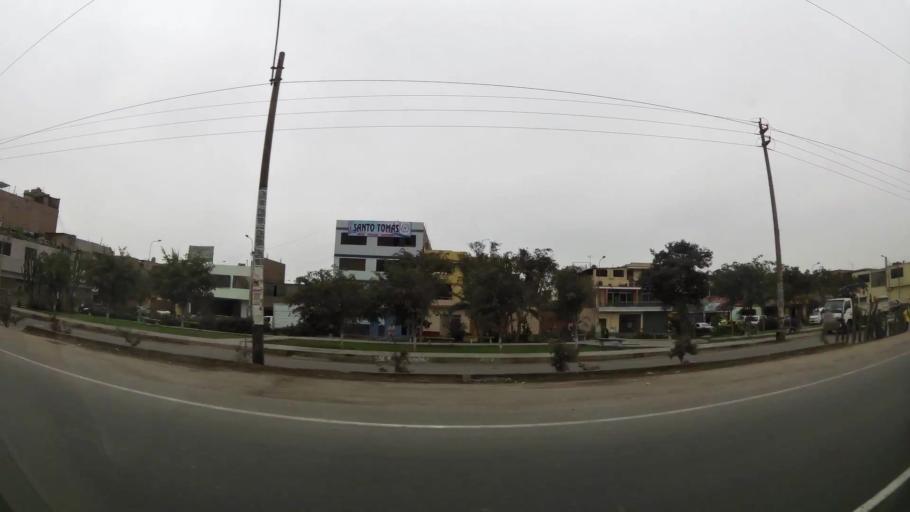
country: PE
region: Lima
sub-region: Lima
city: Urb. Santo Domingo
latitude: -11.9261
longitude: -77.0427
